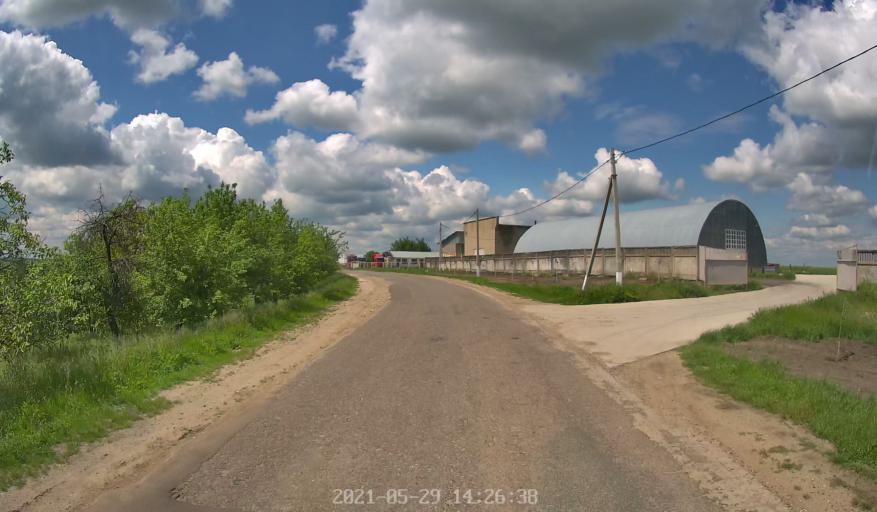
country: MD
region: Hincesti
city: Hincesti
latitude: 46.8450
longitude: 28.6576
